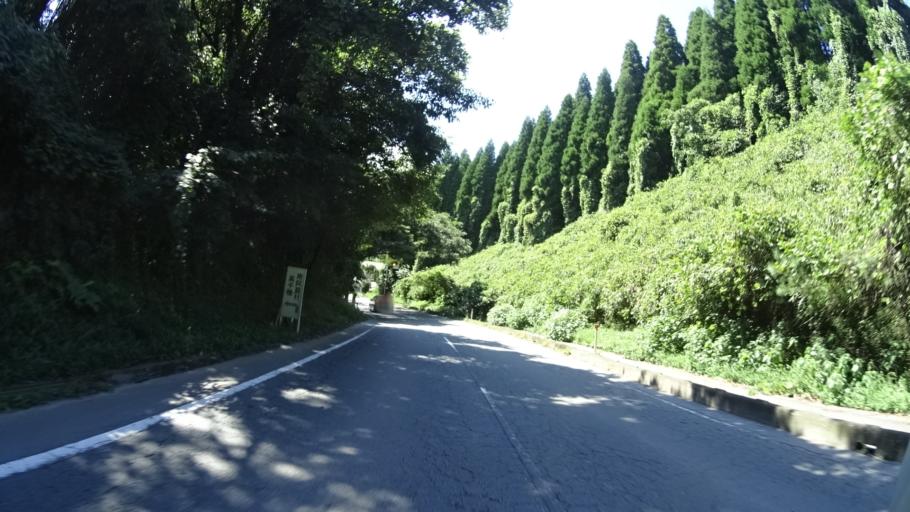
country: JP
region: Kumamoto
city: Aso
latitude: 32.8716
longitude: 130.9960
